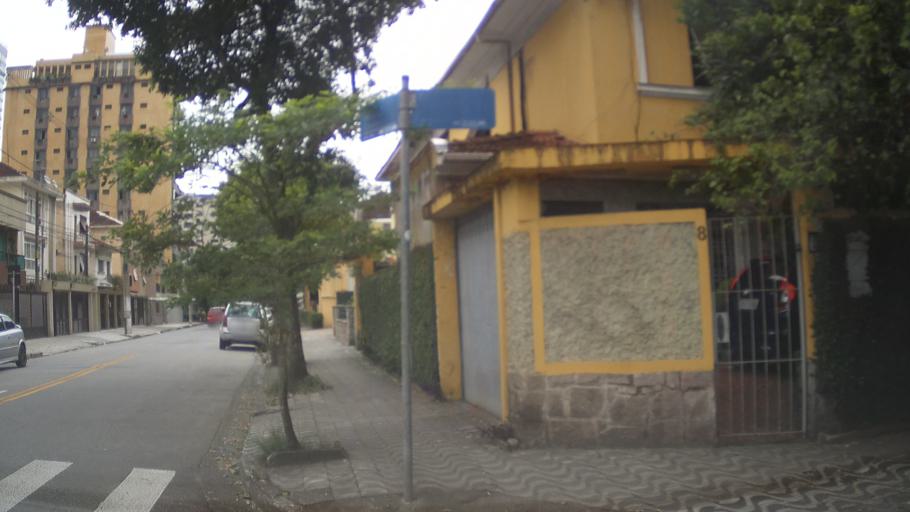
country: BR
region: Sao Paulo
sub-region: Santos
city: Santos
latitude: -23.9687
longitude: -46.3191
